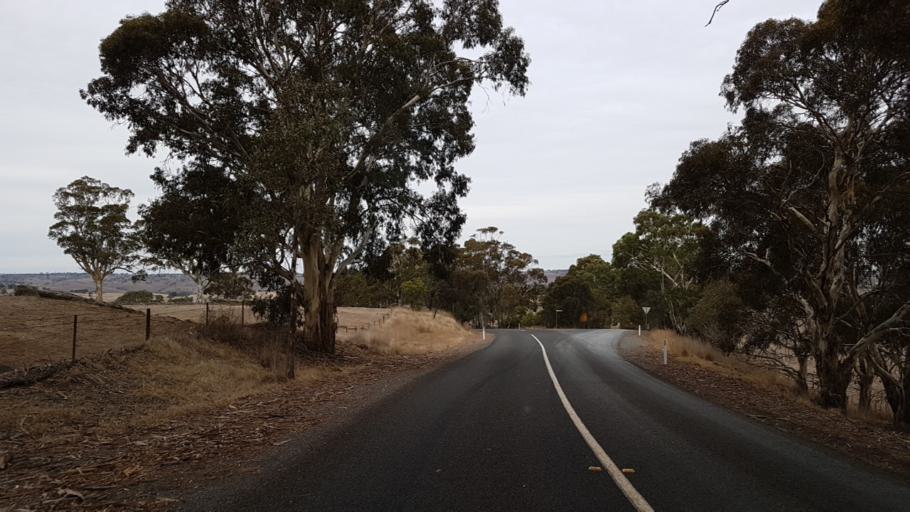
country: AU
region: South Australia
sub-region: Mount Barker
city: Nairne
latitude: -34.9858
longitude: 138.9870
